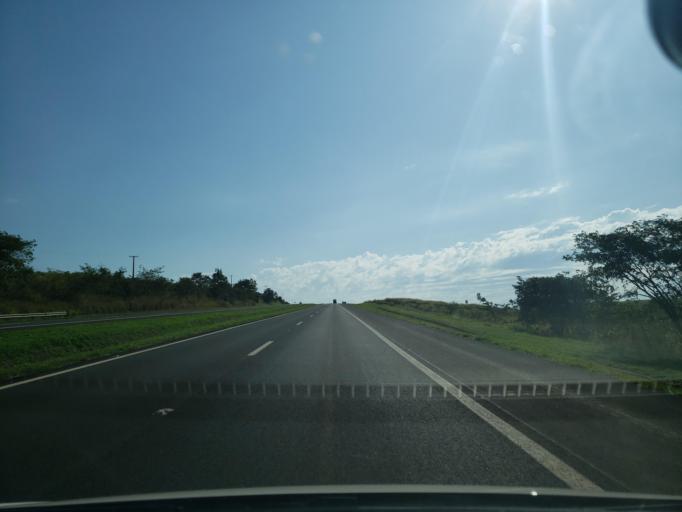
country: BR
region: Sao Paulo
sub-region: Penapolis
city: Penapolis
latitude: -21.5159
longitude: -50.0082
